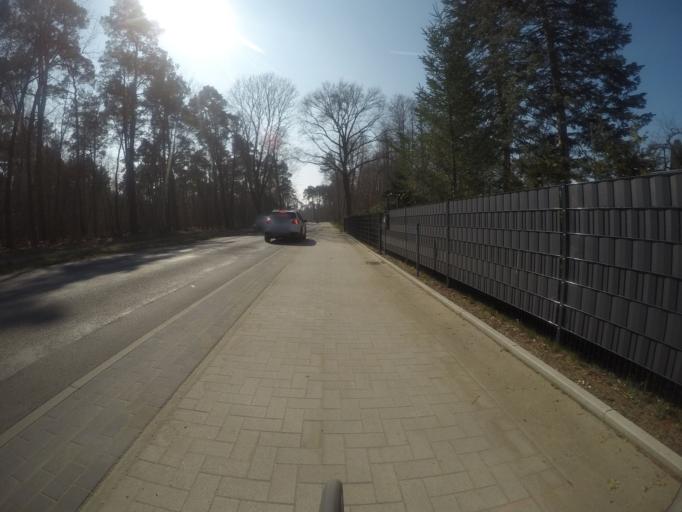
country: DE
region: Berlin
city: Schmockwitz
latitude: 52.3458
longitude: 13.6630
